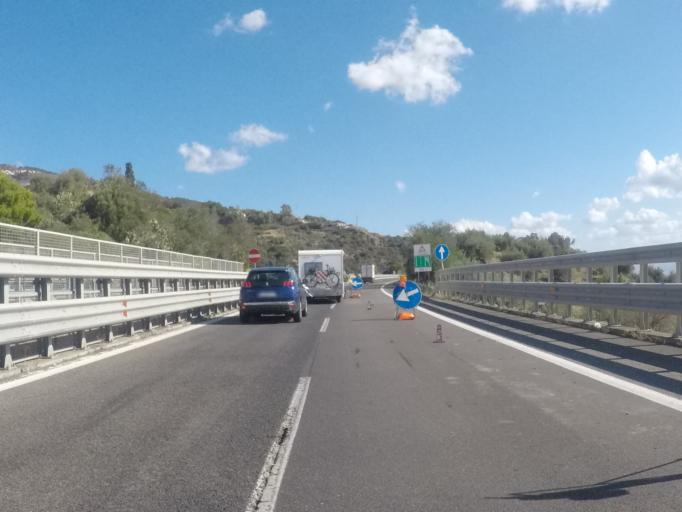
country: IT
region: Sicily
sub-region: Messina
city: Ali Terme
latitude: 38.0061
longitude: 15.4221
